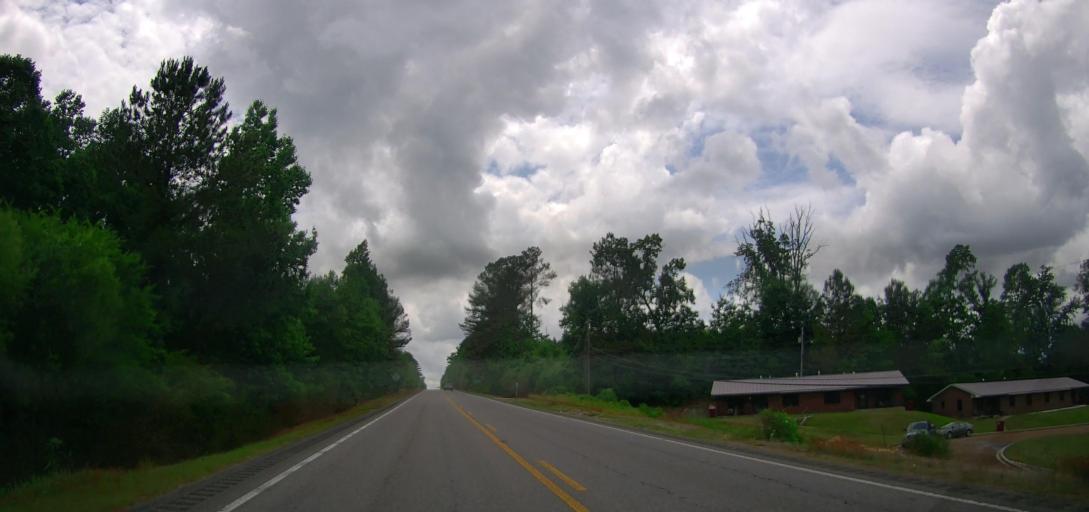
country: US
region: Alabama
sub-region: Marion County
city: Hamilton
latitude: 34.1374
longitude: -88.0042
